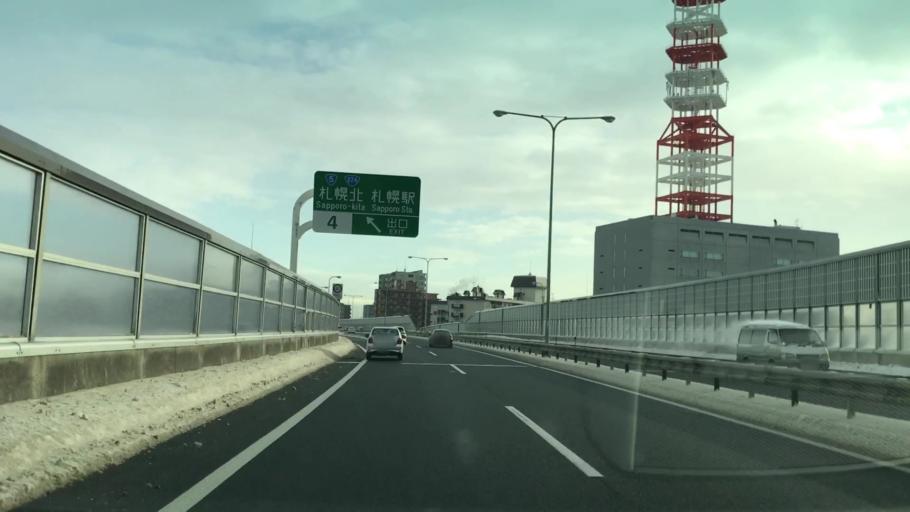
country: JP
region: Hokkaido
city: Sapporo
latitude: 43.1002
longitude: 141.3328
